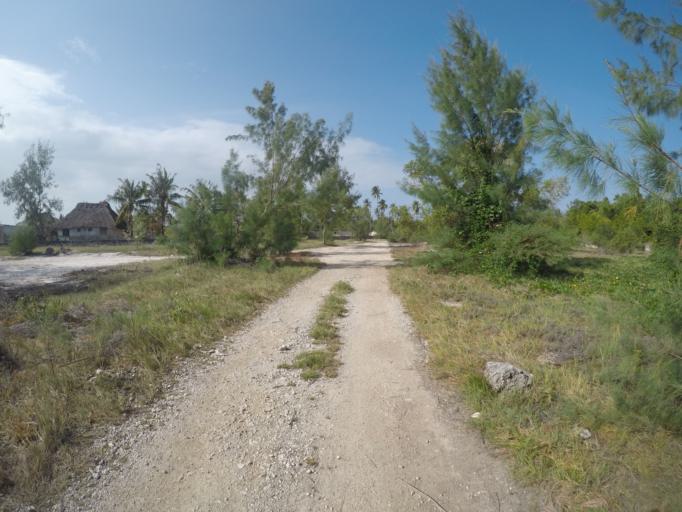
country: TZ
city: Kiwengwa
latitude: -6.1440
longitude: 39.4900
